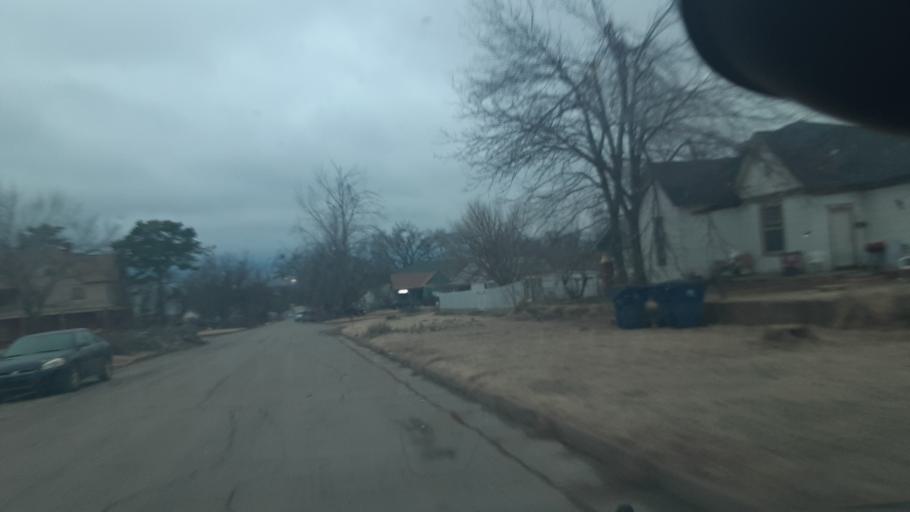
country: US
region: Oklahoma
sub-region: Logan County
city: Guthrie
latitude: 35.8760
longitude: -97.4169
